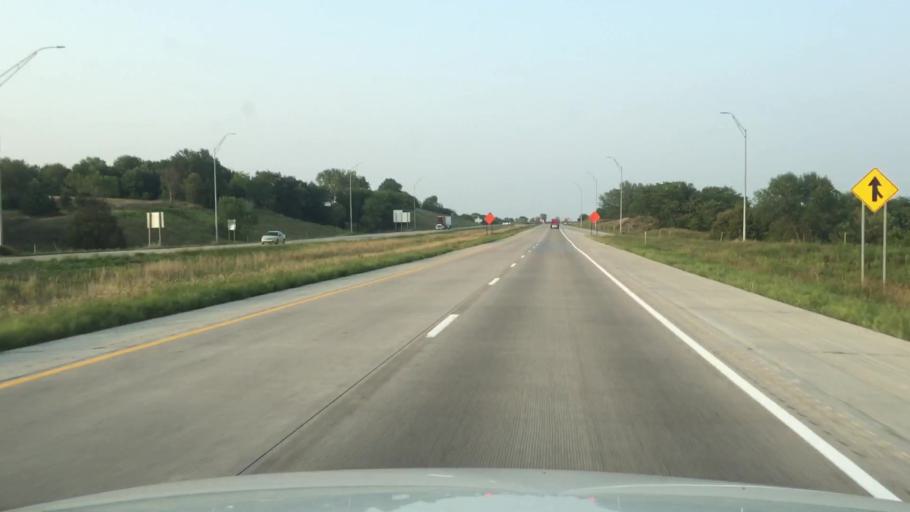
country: US
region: Iowa
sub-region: Decatur County
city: Lamoni
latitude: 40.6259
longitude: -93.8879
